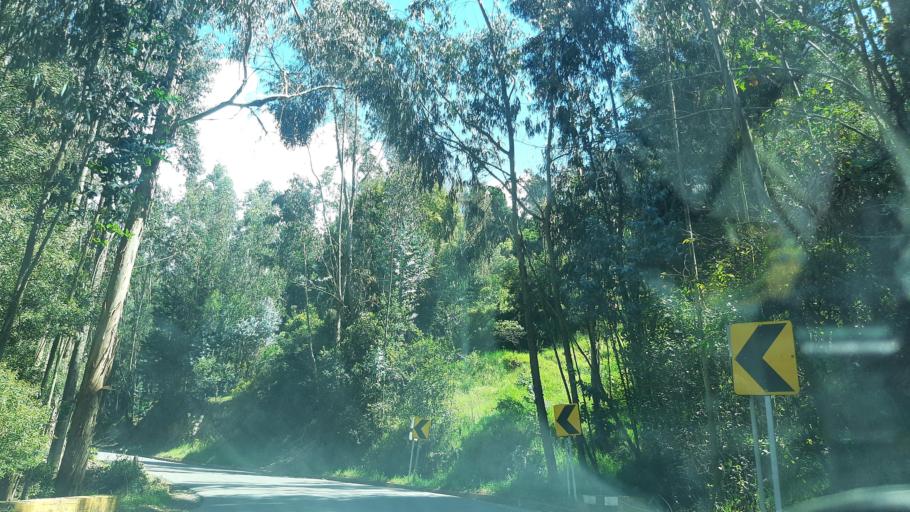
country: CO
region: Boyaca
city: Samaca
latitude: 5.4811
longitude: -73.4774
